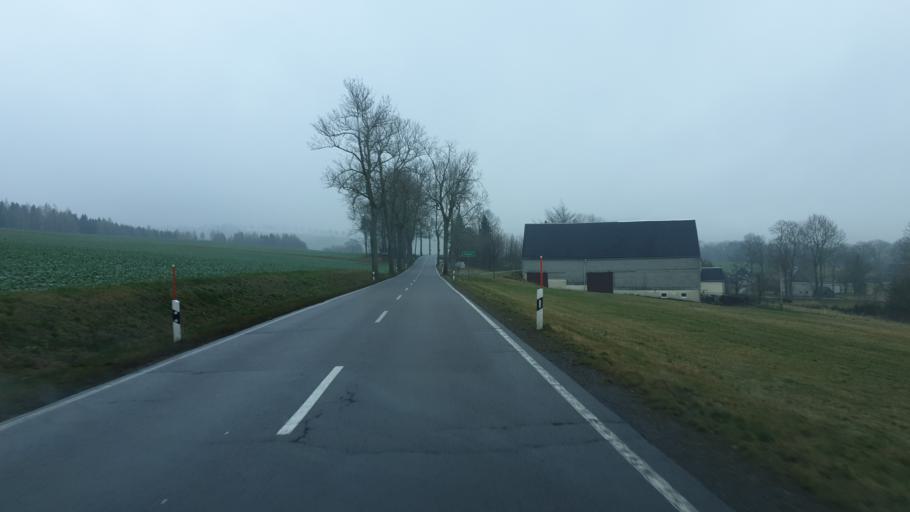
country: DE
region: Saxony
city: Sayda
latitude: 50.7236
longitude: 13.3974
